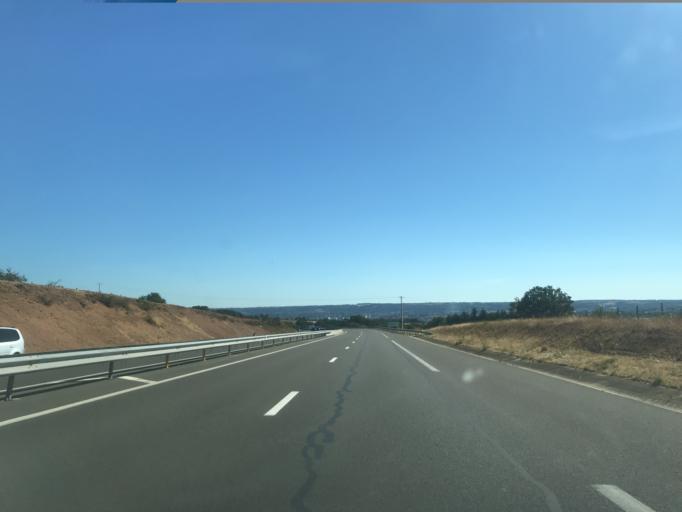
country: FR
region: Auvergne
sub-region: Departement de l'Allier
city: Premilhat
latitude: 46.3242
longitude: 2.5293
